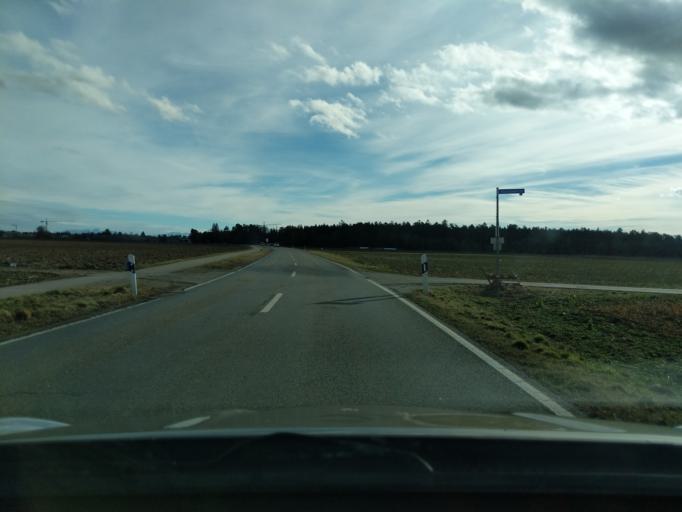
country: DE
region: Bavaria
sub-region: Upper Bavaria
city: Vaterstetten
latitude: 48.1246
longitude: 11.7662
